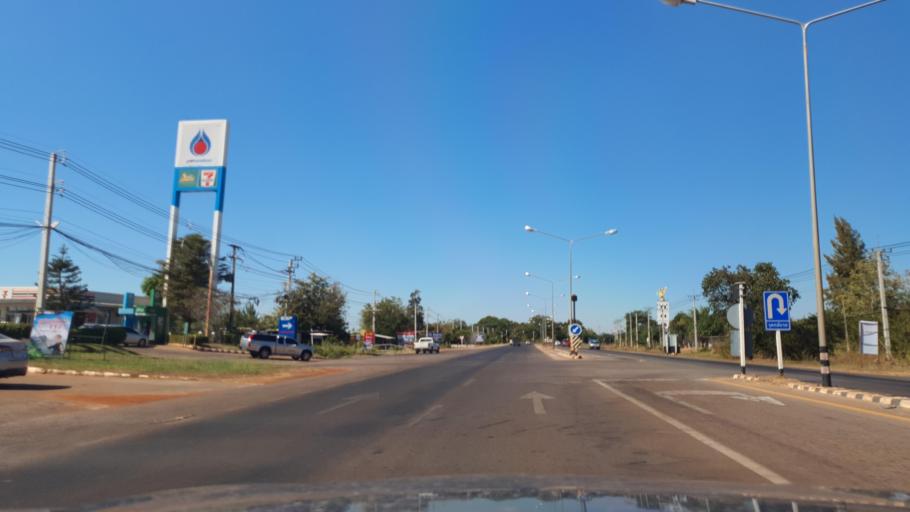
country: TH
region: Sakon Nakhon
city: Sakon Nakhon
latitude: 17.2569
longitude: 104.1671
